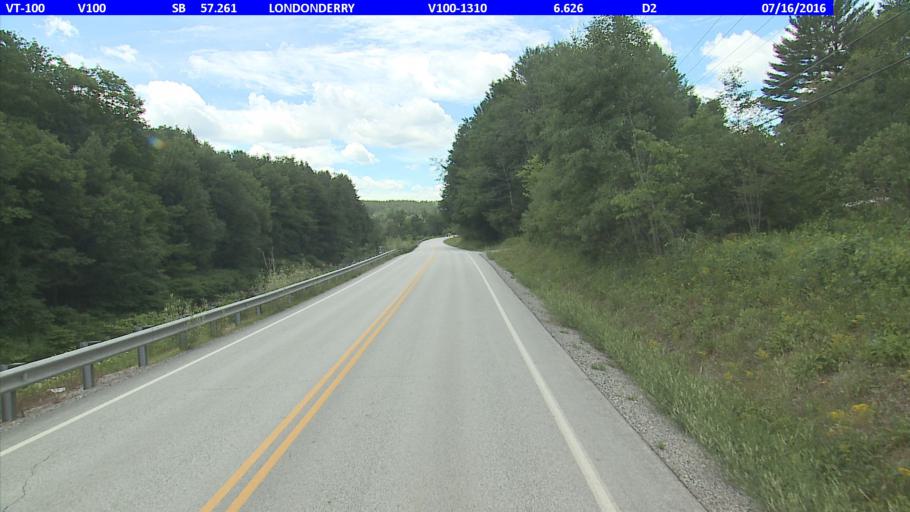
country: US
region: Vermont
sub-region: Windsor County
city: Chester
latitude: 43.2352
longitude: -72.7976
